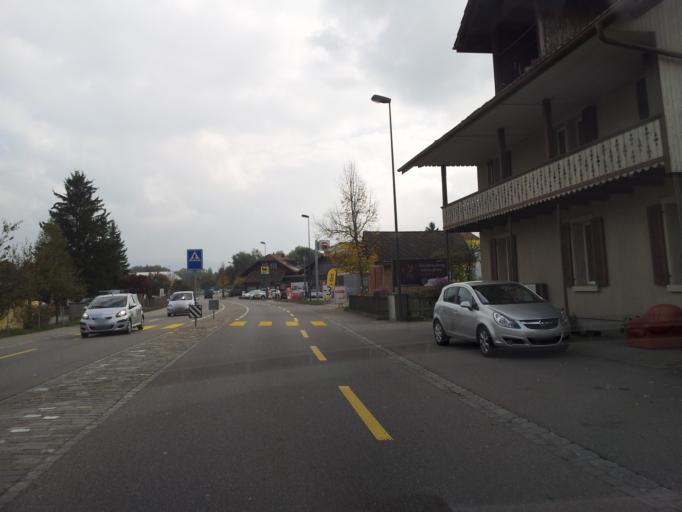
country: CH
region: Bern
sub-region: Bern-Mittelland District
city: Belp
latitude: 46.8896
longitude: 7.5204
